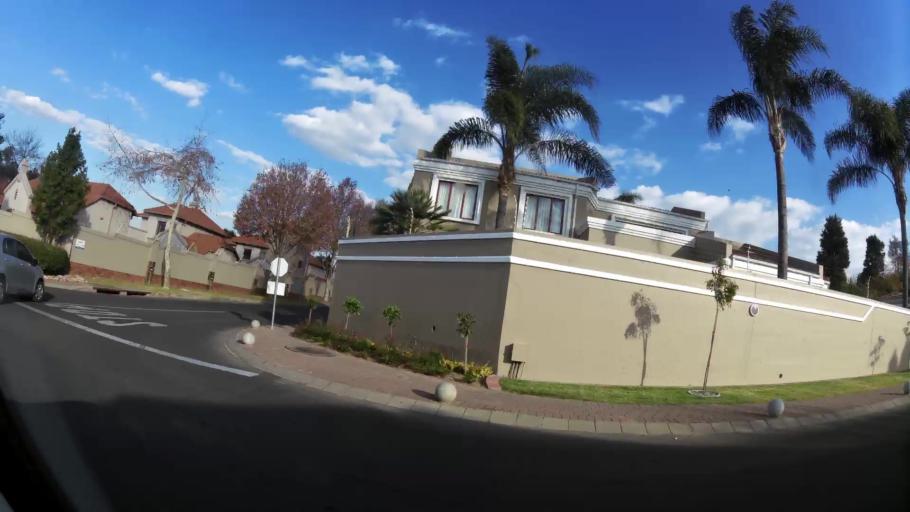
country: ZA
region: Gauteng
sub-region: City of Johannesburg Metropolitan Municipality
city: Diepsloot
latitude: -26.0206
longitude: 28.0192
